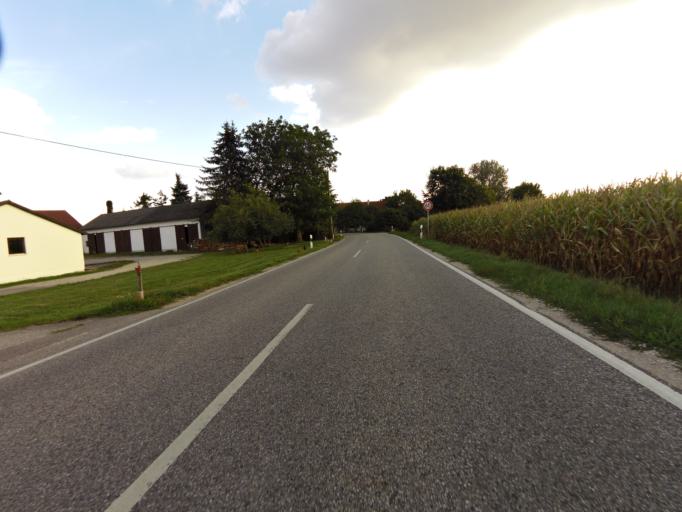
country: DE
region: Bavaria
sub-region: Upper Bavaria
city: Wang
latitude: 48.4869
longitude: 11.9604
